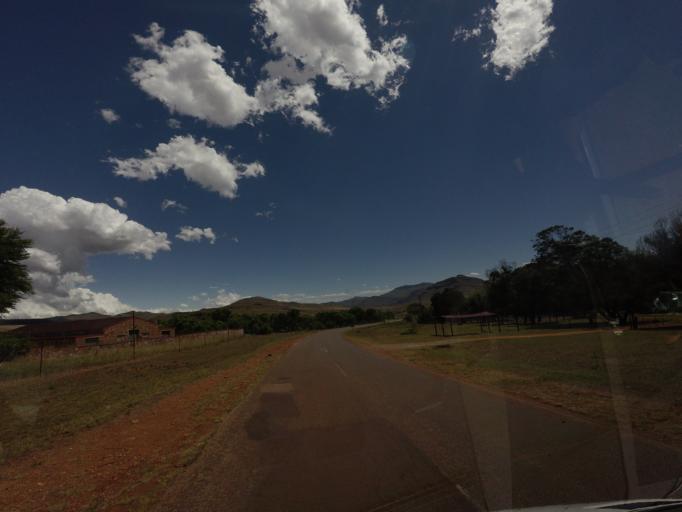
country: ZA
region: Mpumalanga
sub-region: Ehlanzeni District
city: Graksop
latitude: -24.6696
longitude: 30.8090
